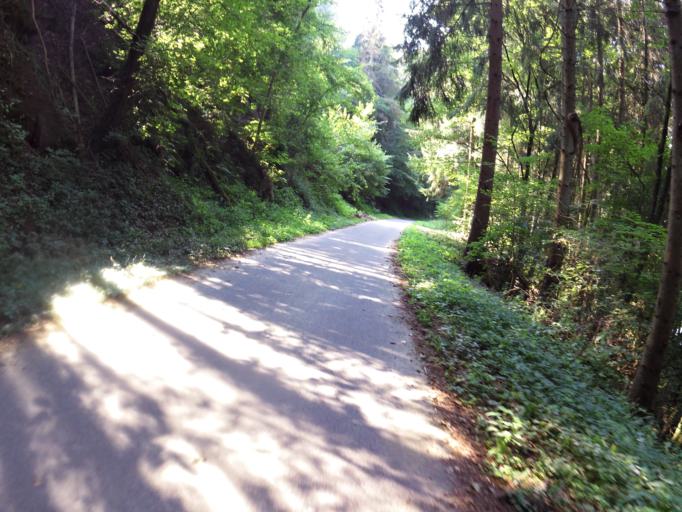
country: DE
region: Rheinland-Pfalz
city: Preist
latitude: 49.9237
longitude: 6.6218
